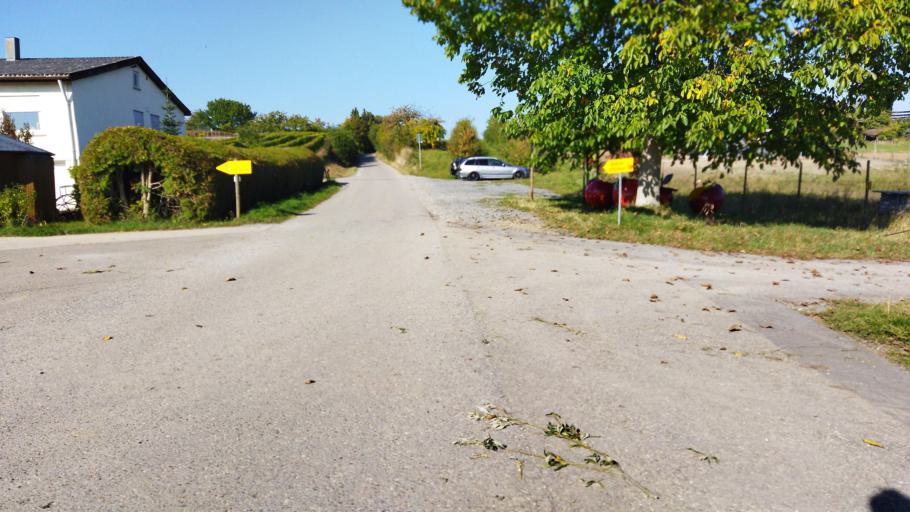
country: DE
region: Baden-Wuerttemberg
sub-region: Regierungsbezirk Stuttgart
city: Erligheim
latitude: 49.0158
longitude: 9.0880
